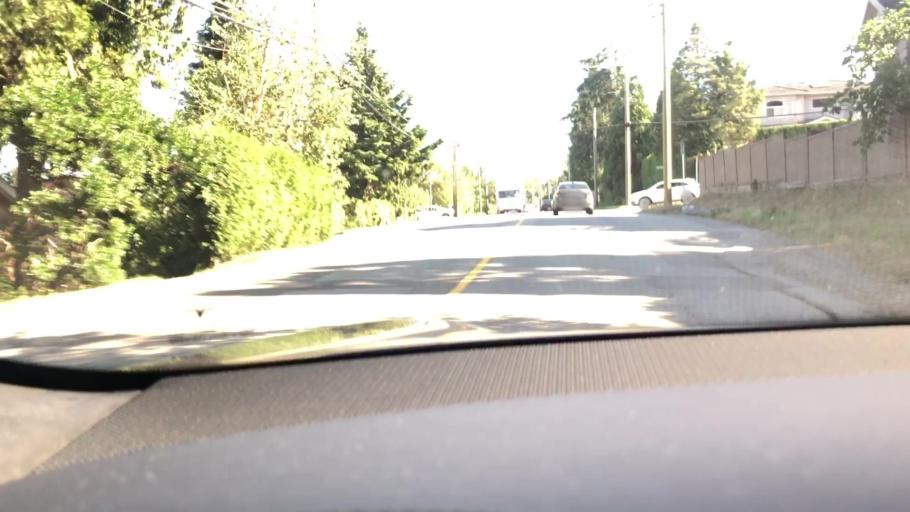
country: CA
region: British Columbia
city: Burnaby
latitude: 49.2522
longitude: -122.9818
